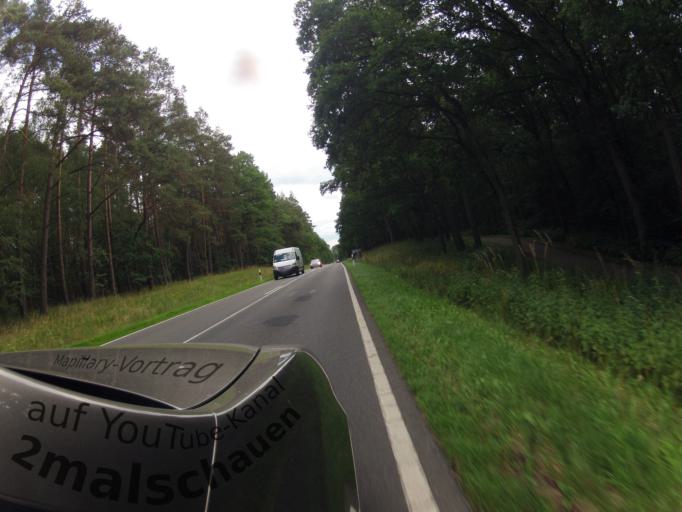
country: DE
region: Mecklenburg-Vorpommern
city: Lassan
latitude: 53.8888
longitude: 13.7893
